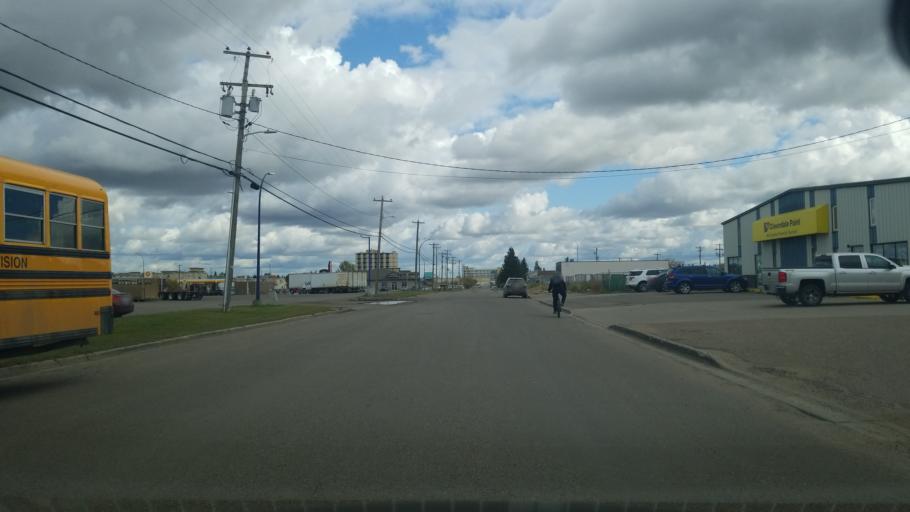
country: CA
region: Saskatchewan
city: Lloydminster
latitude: 53.2769
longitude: -110.0280
